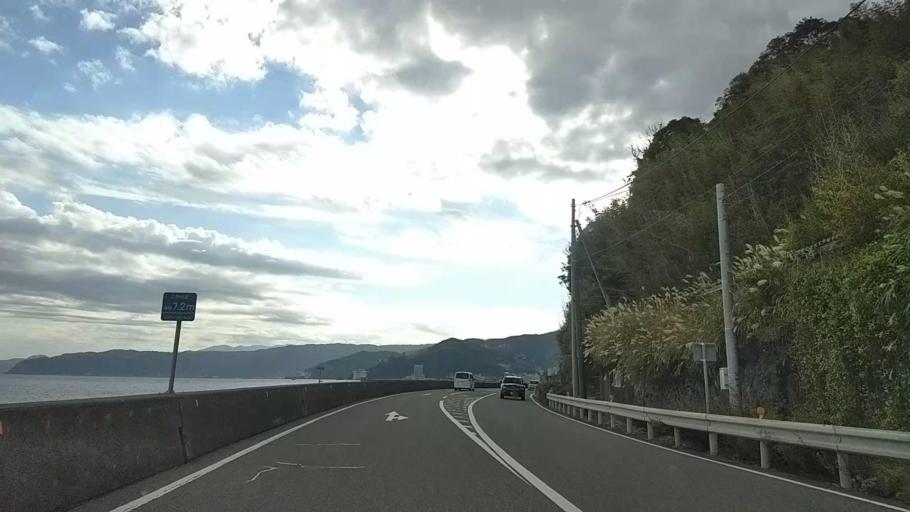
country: JP
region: Shizuoka
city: Atami
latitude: 35.1184
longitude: 139.0980
